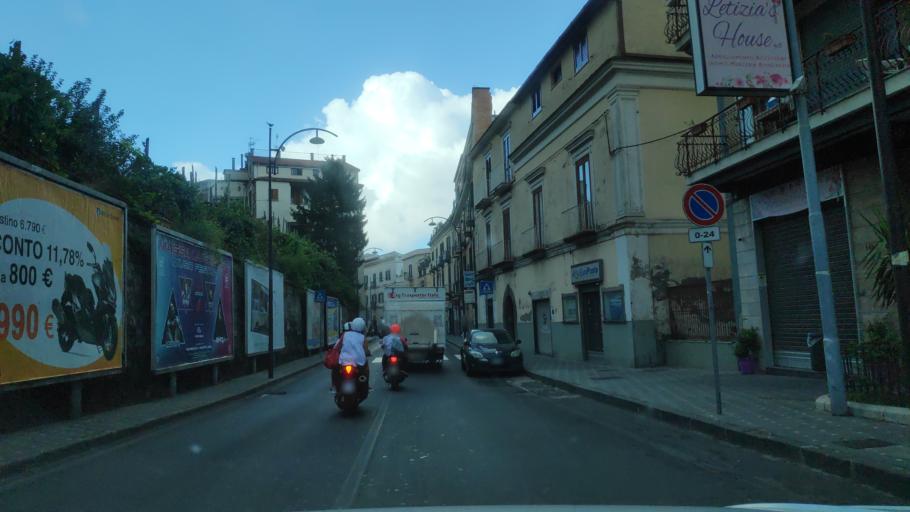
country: IT
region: Campania
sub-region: Provincia di Napoli
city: Meta
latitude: 40.6394
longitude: 14.4188
